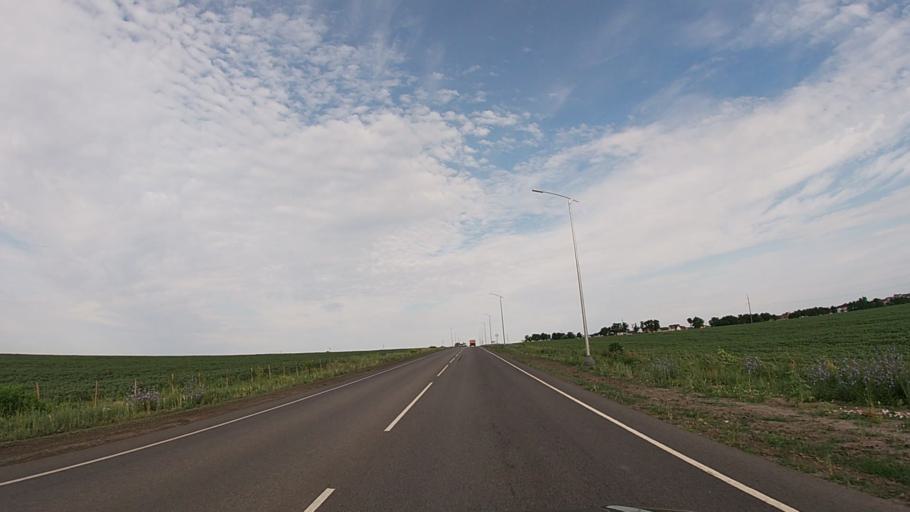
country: RU
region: Belgorod
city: Severnyy
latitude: 50.6649
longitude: 36.5092
